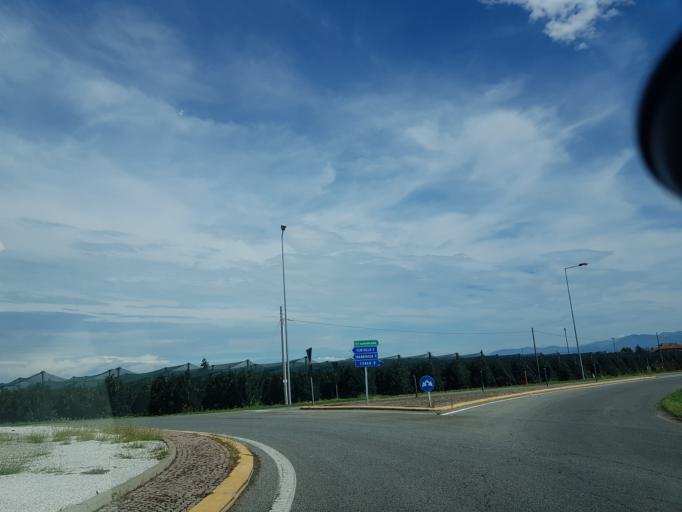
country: IT
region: Piedmont
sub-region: Provincia di Cuneo
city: Roata Rossi
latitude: 44.4711
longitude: 7.5112
